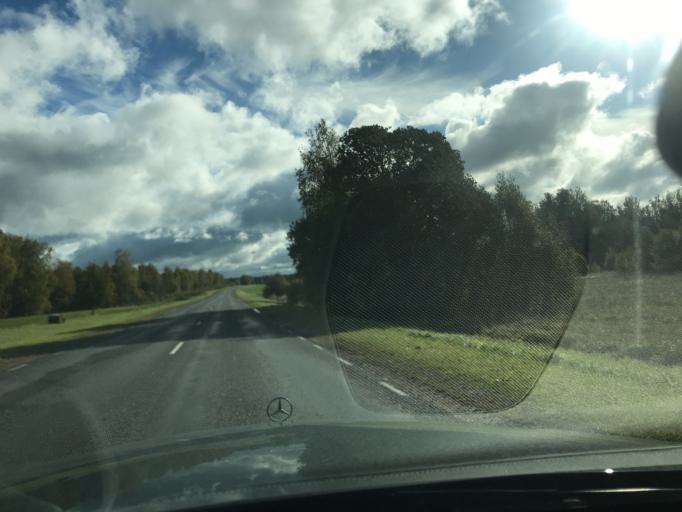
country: EE
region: Tartu
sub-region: Elva linn
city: Elva
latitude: 58.0085
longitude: 26.2526
